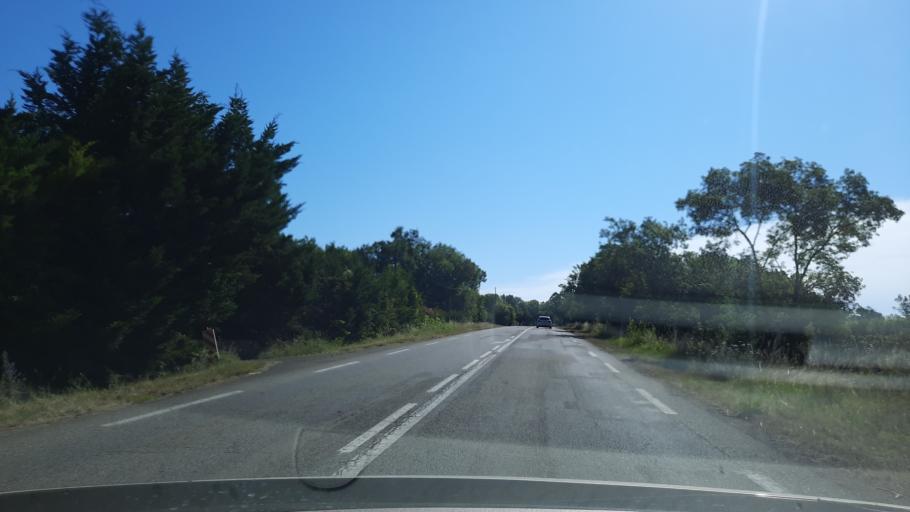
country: FR
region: Midi-Pyrenees
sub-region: Departement du Tarn-et-Garonne
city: Monteils
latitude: 44.1706
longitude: 1.5896
